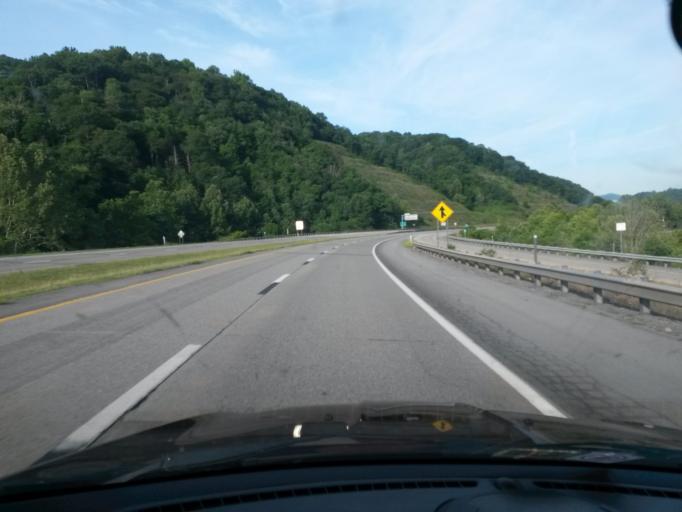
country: US
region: West Virginia
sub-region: Summers County
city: Hinton
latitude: 37.8056
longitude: -80.8172
